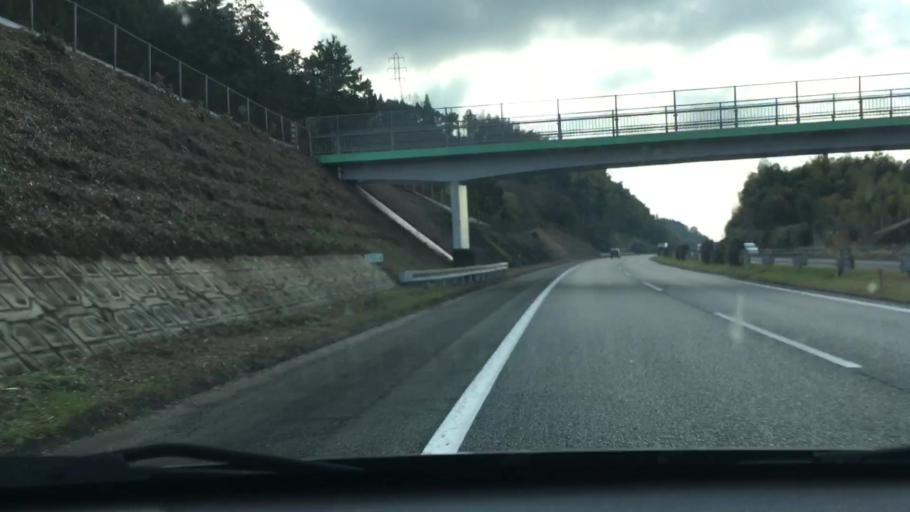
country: JP
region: Kumamoto
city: Yatsushiro
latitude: 32.5331
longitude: 130.6708
